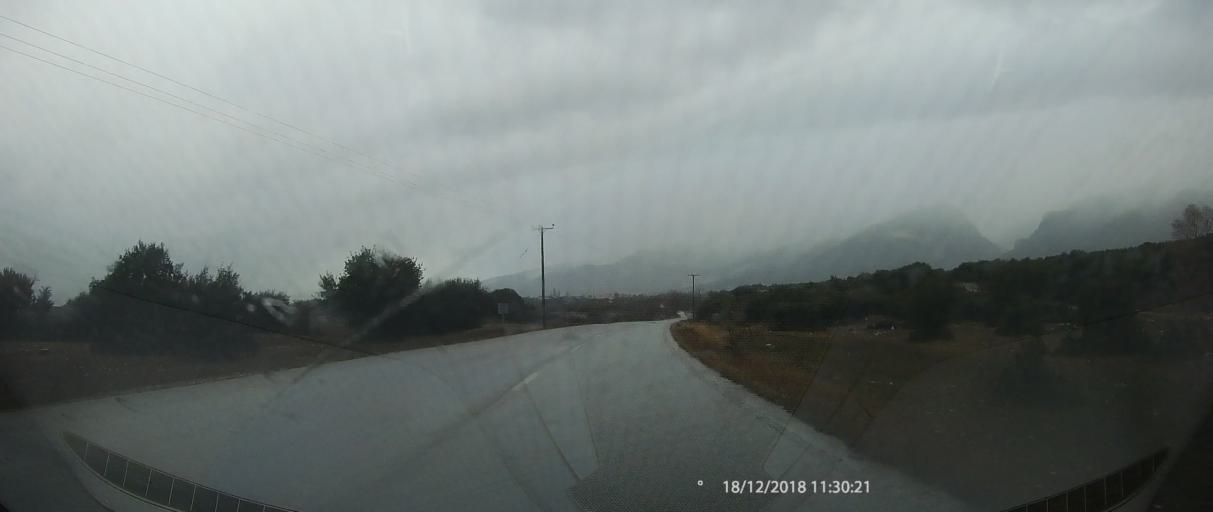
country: GR
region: Central Macedonia
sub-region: Nomos Pierias
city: Litochoro
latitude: 40.1240
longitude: 22.5223
